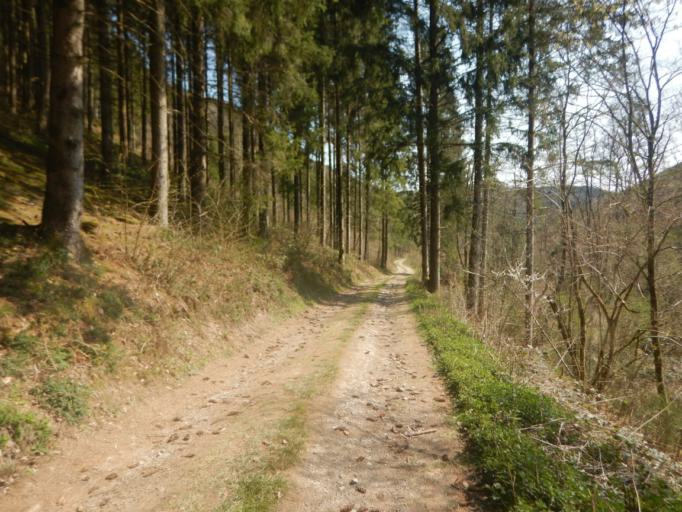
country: LU
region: Diekirch
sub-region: Canton de Clervaux
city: Clervaux
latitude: 50.0418
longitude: 6.0063
